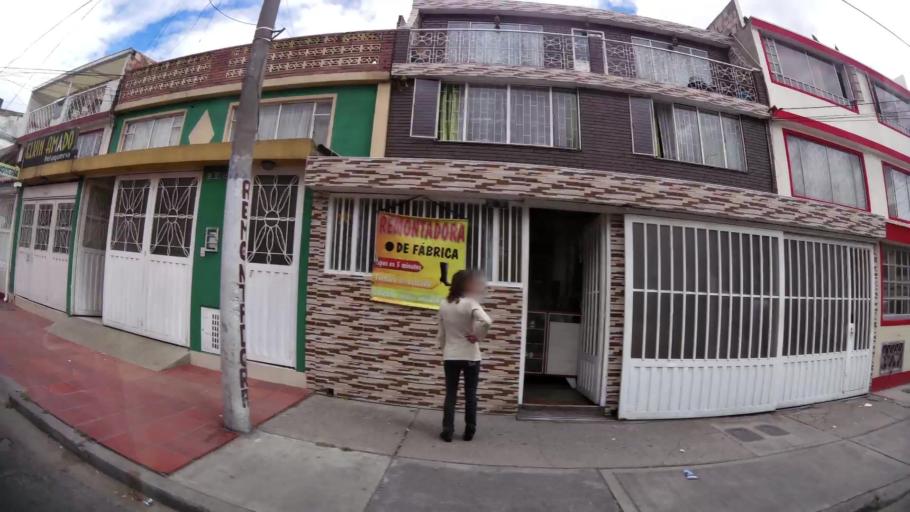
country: CO
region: Bogota D.C.
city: Bogota
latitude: 4.5980
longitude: -74.1222
